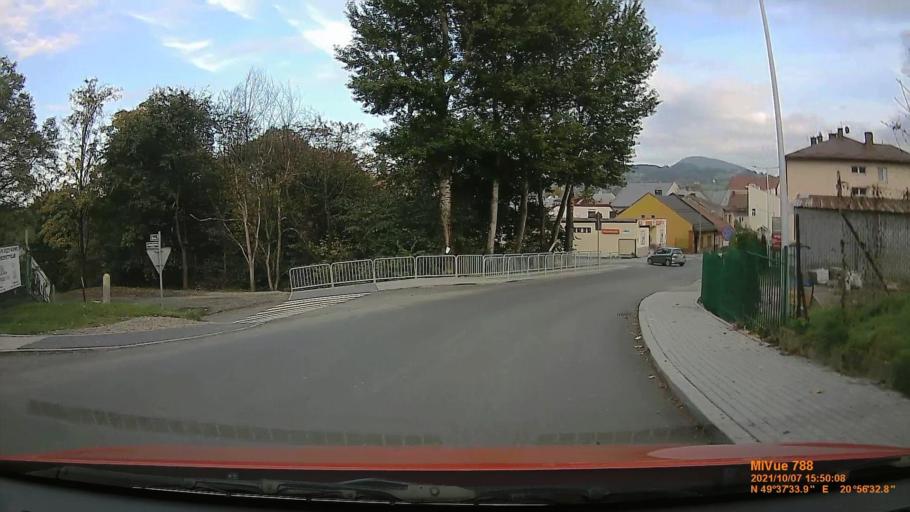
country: PL
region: Lesser Poland Voivodeship
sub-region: Powiat nowosadecki
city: Grybow
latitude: 49.6261
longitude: 20.9423
